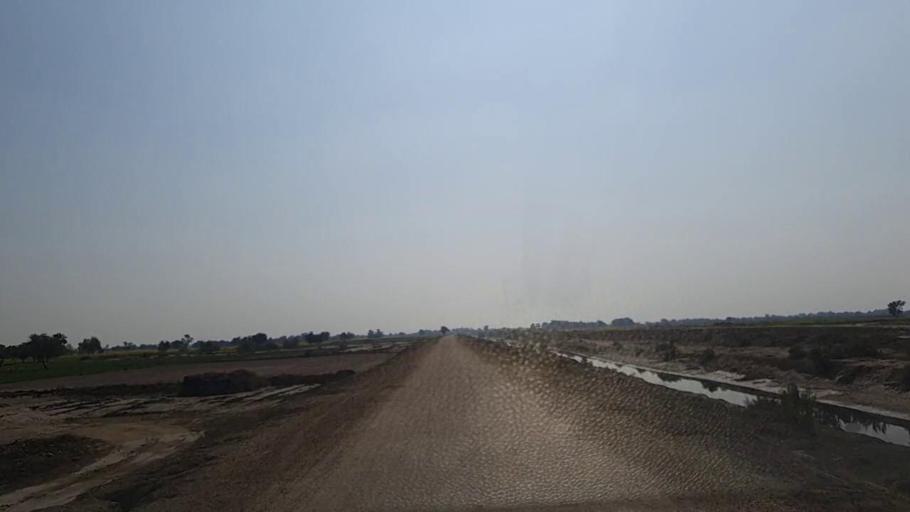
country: PK
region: Sindh
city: Nawabshah
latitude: 26.2639
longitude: 68.5031
